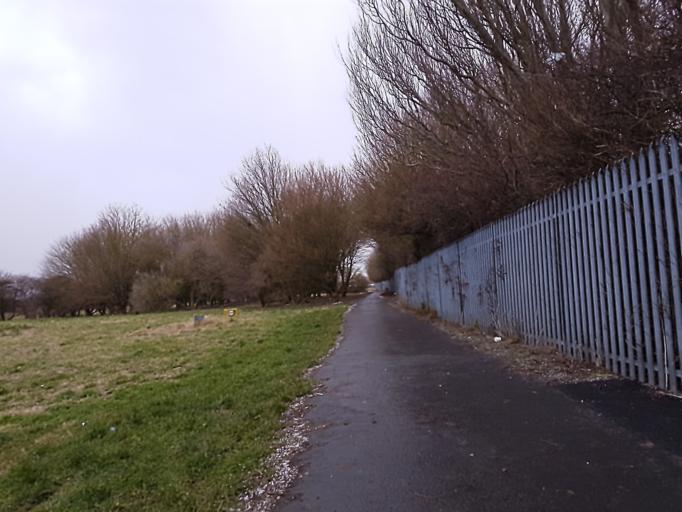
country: GB
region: England
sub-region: North East Lincolnshire
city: Great Coates
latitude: 53.5652
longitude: -0.1191
